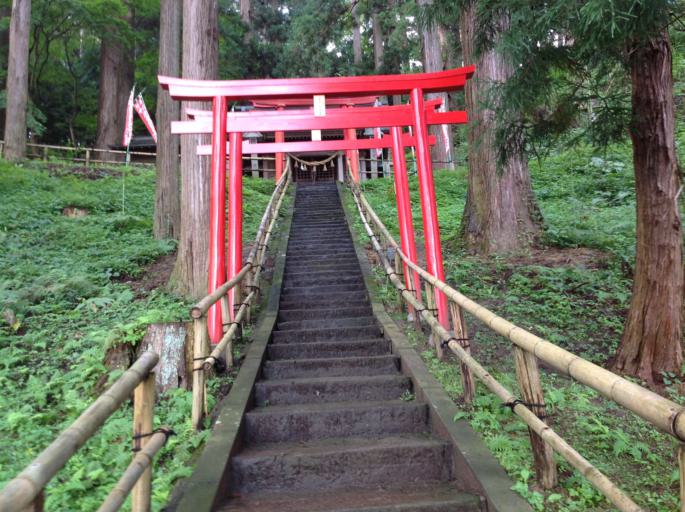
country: JP
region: Iwate
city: Ichinoseki
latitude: 39.0001
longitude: 141.1066
